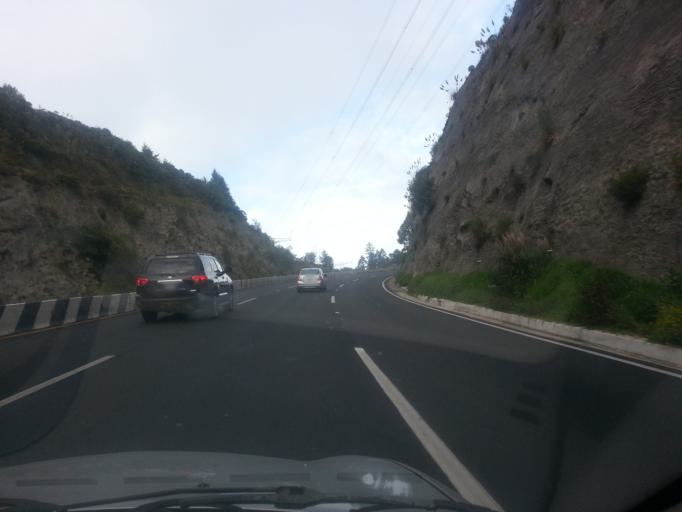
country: MX
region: Mexico City
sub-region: Cuajimalpa de Morelos
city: San Lorenzo Acopilco
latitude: 19.2971
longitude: -99.3494
